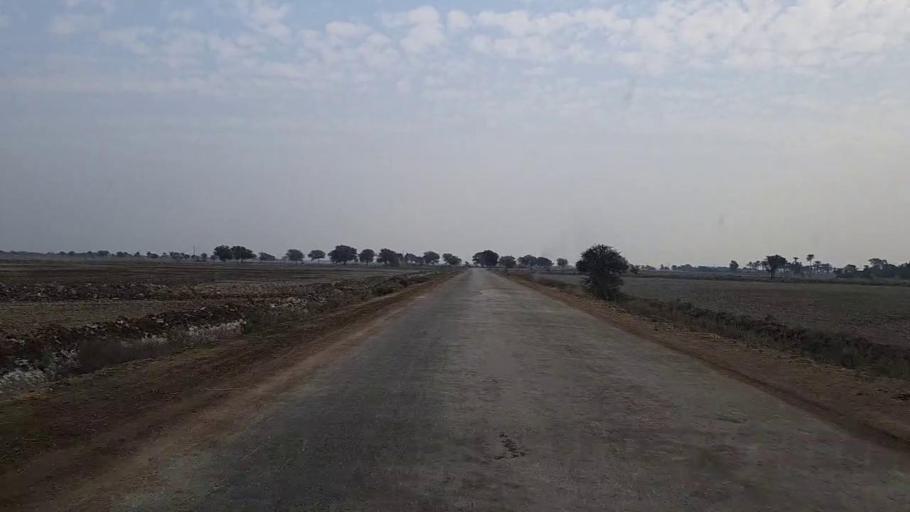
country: PK
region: Sindh
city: Mirwah Gorchani
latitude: 25.3924
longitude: 69.0791
